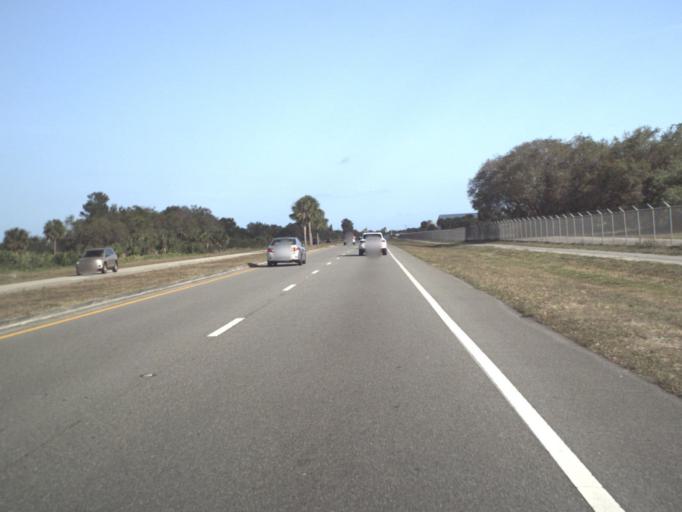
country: US
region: Florida
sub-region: Brevard County
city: Melbourne
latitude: 28.1107
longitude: -80.6328
